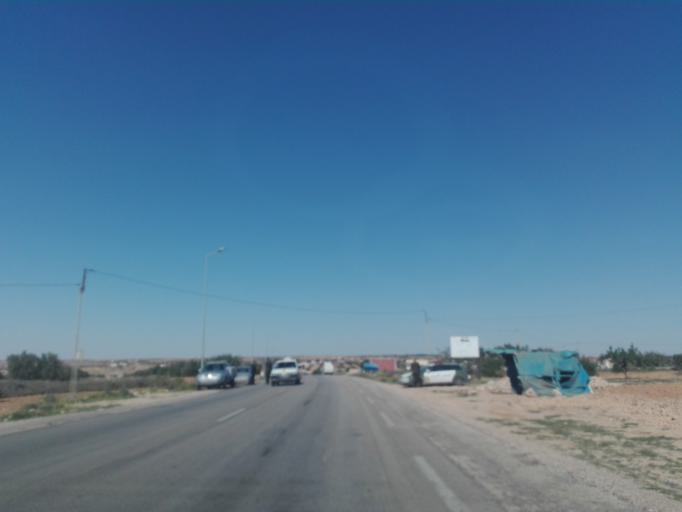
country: TN
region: Safaqis
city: Bi'r `Ali Bin Khalifah
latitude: 34.7409
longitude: 10.3881
